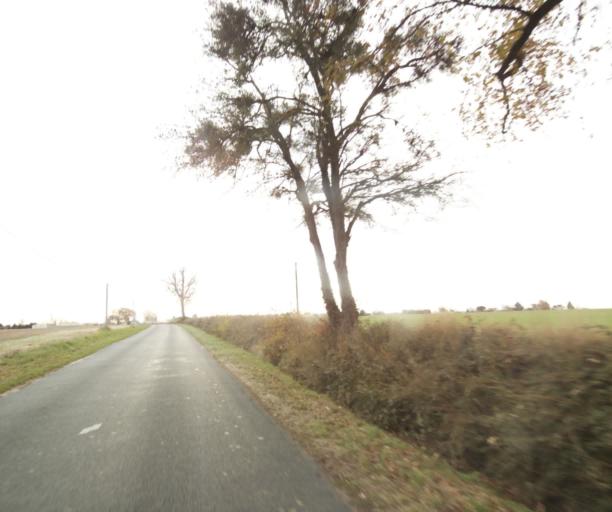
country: FR
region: Poitou-Charentes
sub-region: Departement de la Charente-Maritime
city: Corme-Royal
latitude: 45.7525
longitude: -0.8047
